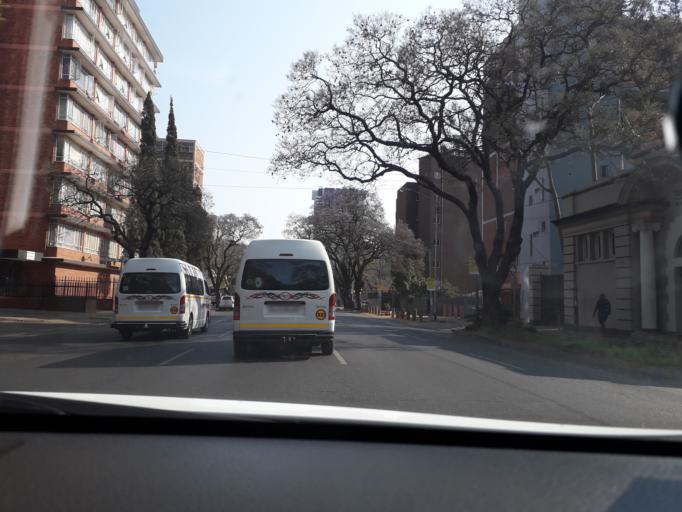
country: ZA
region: Gauteng
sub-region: City of Tshwane Metropolitan Municipality
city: Pretoria
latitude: -25.7530
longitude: 28.1935
